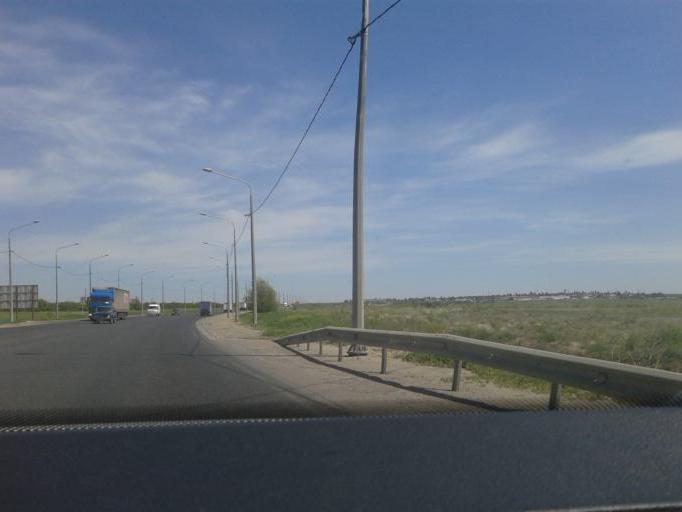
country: RU
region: Volgograd
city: Vodstroy
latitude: 48.8242
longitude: 44.5264
